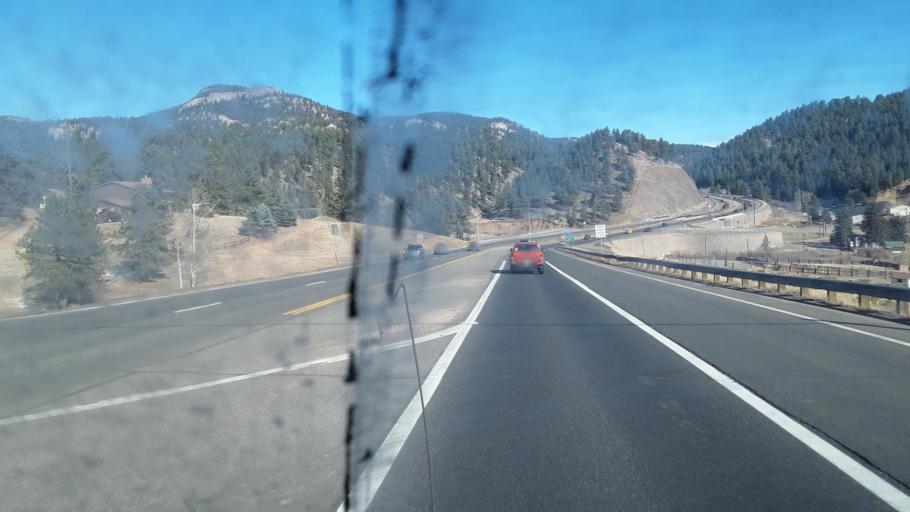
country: US
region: Colorado
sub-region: Jefferson County
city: Evergreen
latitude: 39.4770
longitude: -105.3724
